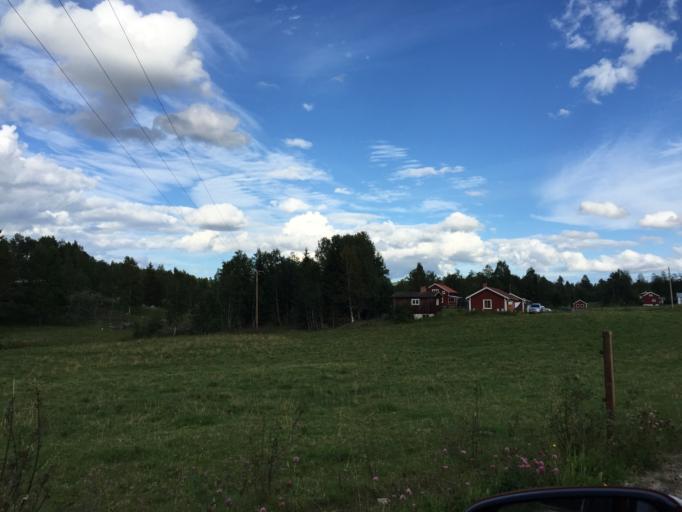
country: SE
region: Gaevleborg
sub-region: Ljusdals Kommun
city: Jaervsoe
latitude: 61.7539
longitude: 16.1988
